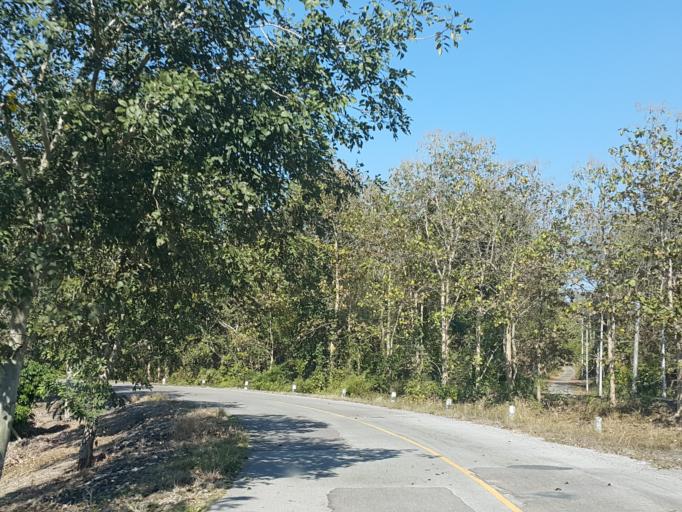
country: TH
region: Chiang Mai
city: Mae Taeng
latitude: 19.0986
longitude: 98.9529
